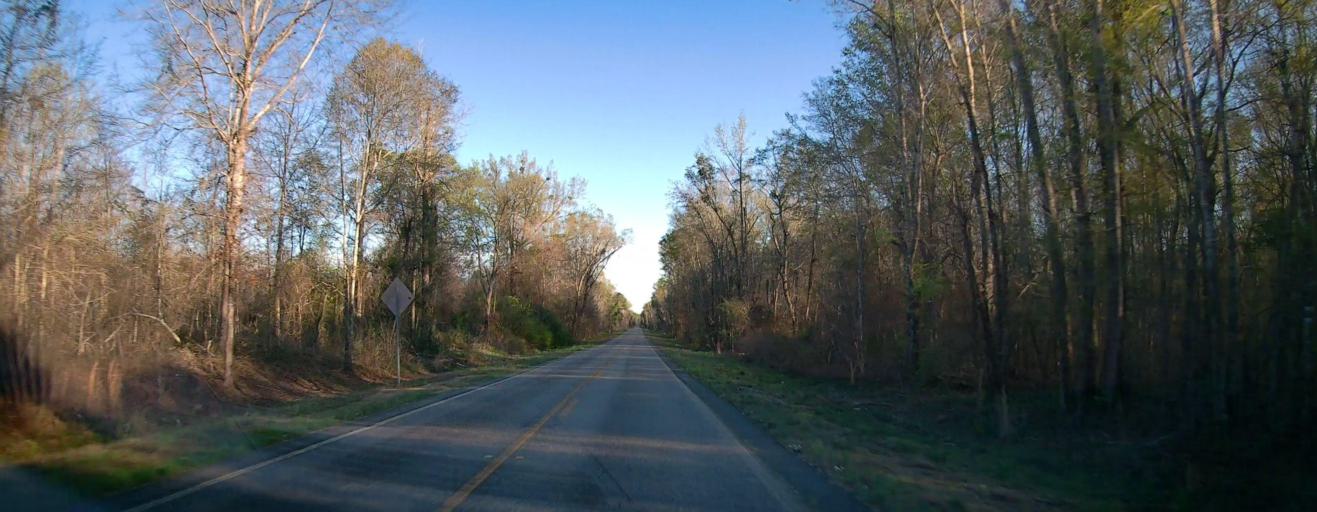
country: US
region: Georgia
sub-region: Wilcox County
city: Abbeville
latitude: 32.1014
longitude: -83.3048
